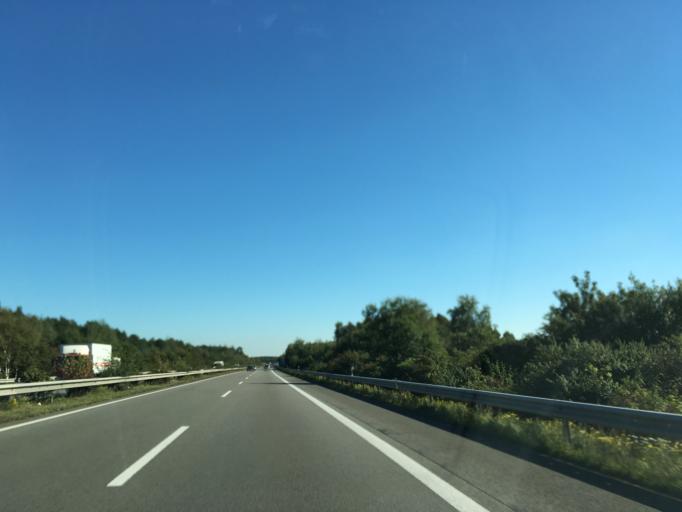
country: DE
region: Lower Saxony
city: Radbruch
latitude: 53.3345
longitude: 10.2522
